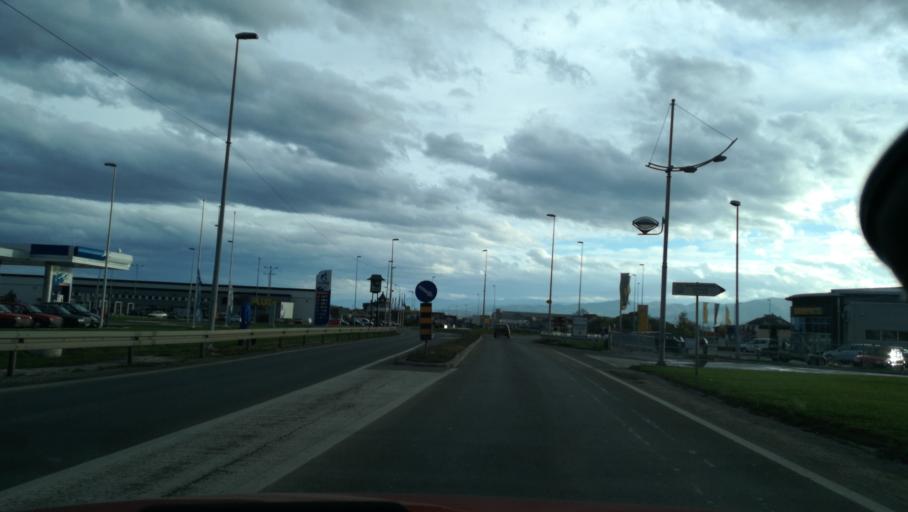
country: RS
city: Prislonica
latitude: 43.9135
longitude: 20.4076
